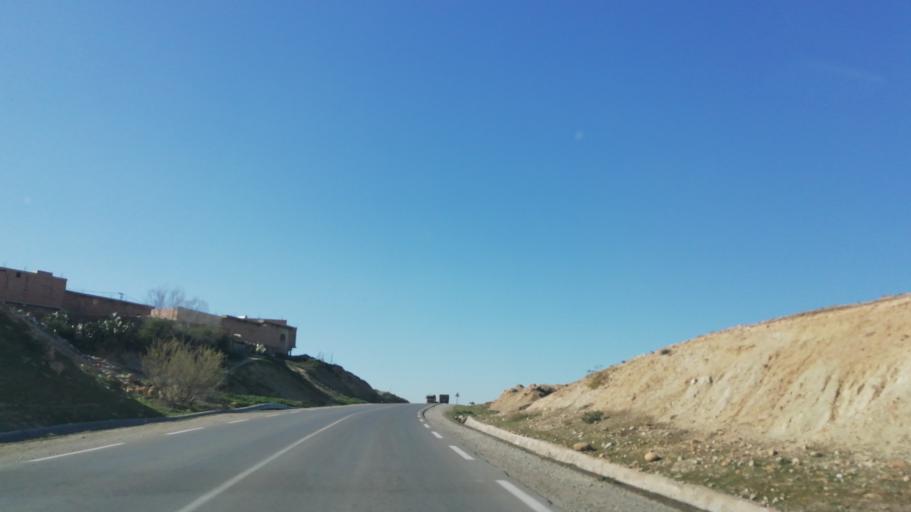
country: DZ
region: Mascara
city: Oued el Abtal
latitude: 35.4559
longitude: 0.7104
